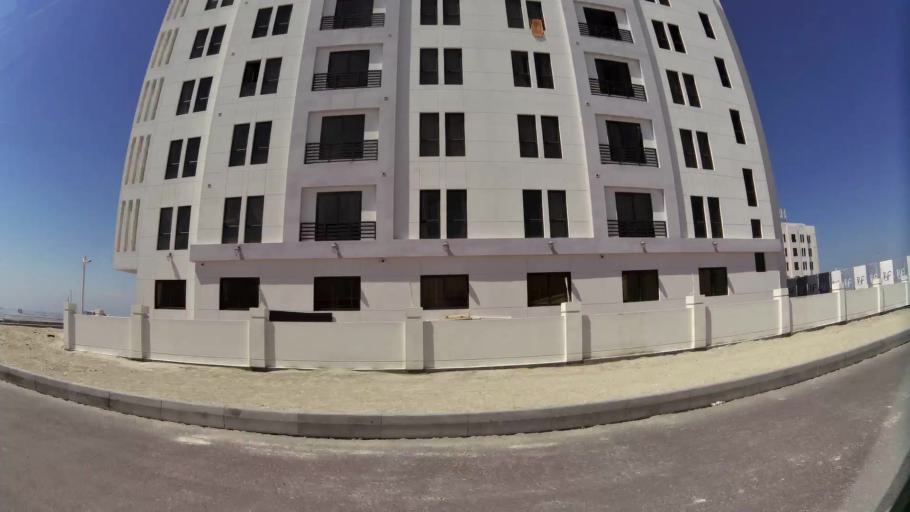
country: BH
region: Muharraq
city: Al Muharraq
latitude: 26.3070
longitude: 50.6224
